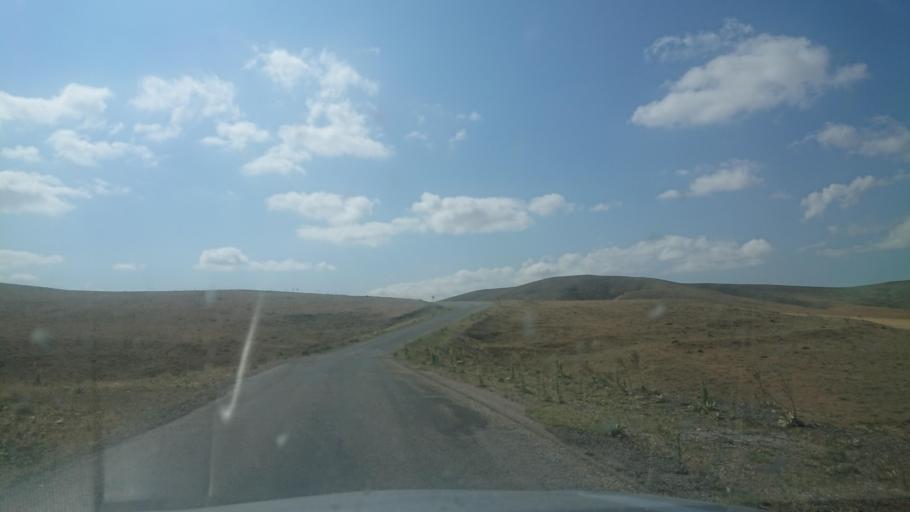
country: TR
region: Aksaray
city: Sariyahsi
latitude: 39.0067
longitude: 33.9566
